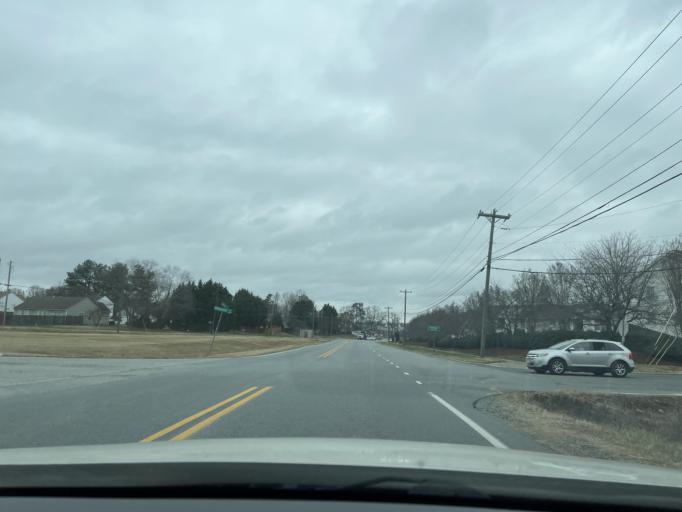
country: US
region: North Carolina
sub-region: Guilford County
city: Pleasant Garden
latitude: 36.0013
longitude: -79.8059
